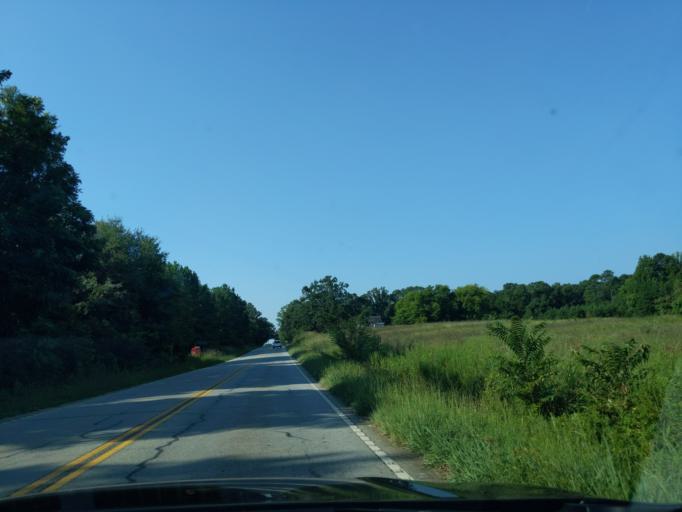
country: US
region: South Carolina
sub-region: Newberry County
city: Prosperity
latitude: 34.1884
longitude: -81.5309
